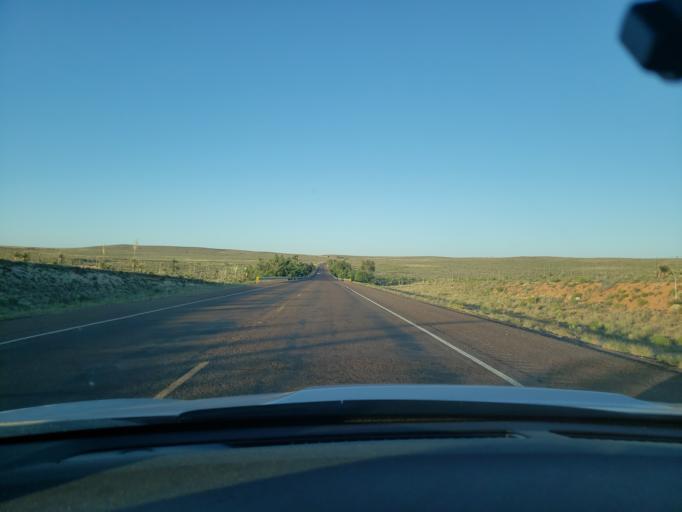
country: US
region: Texas
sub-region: El Paso County
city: Homestead Meadows South
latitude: 31.8301
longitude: -105.8681
